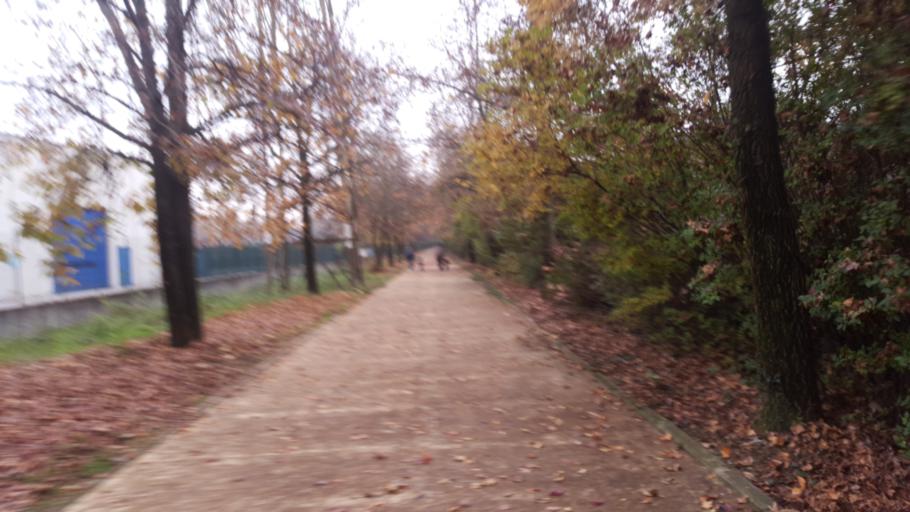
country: IT
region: Lombardy
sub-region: Provincia di Como
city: Novedrate
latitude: 45.6931
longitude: 9.1311
